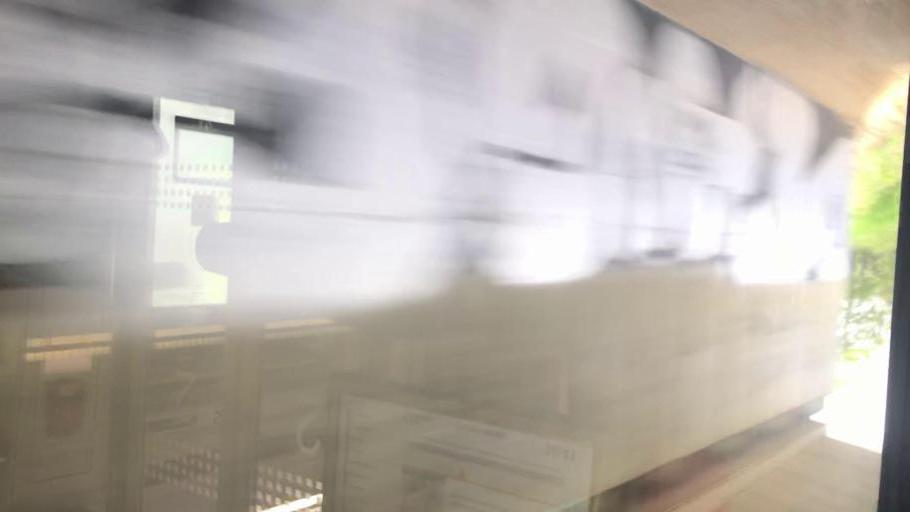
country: PL
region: Lower Silesian Voivodeship
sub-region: Powiat wroclawski
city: Katy Wroclawskie
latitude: 51.0236
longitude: 16.7079
